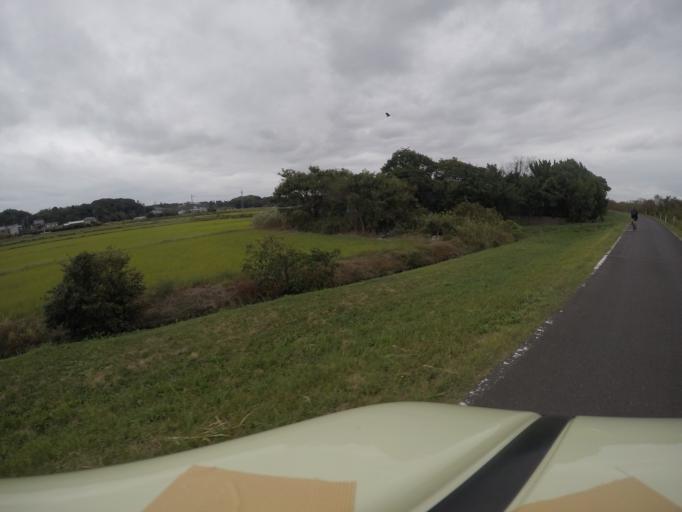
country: JP
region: Ibaraki
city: Inashiki
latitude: 35.9823
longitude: 140.3827
